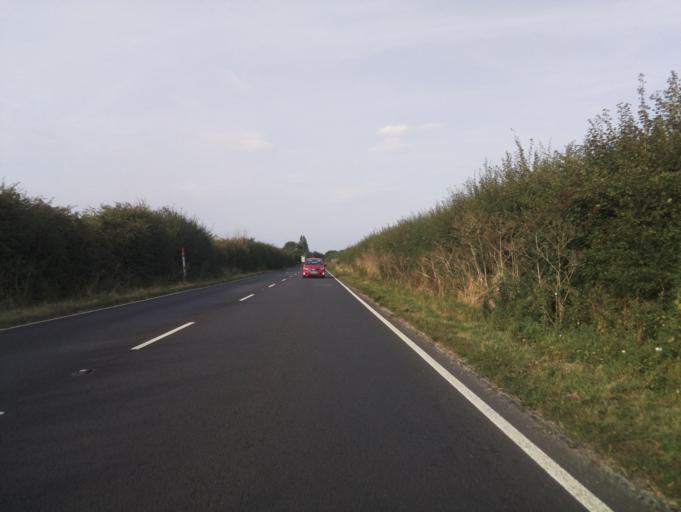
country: GB
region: England
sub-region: Gloucestershire
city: Gotherington
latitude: 52.0000
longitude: -2.0574
